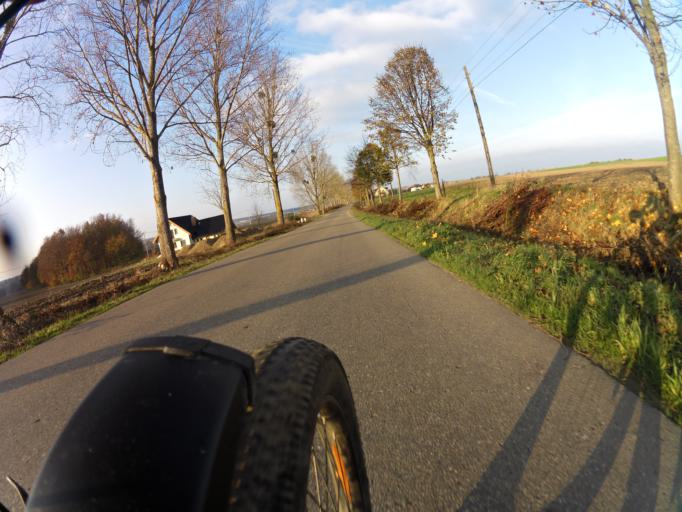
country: PL
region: Pomeranian Voivodeship
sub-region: Powiat pucki
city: Krokowa
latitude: 54.7691
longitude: 18.1793
